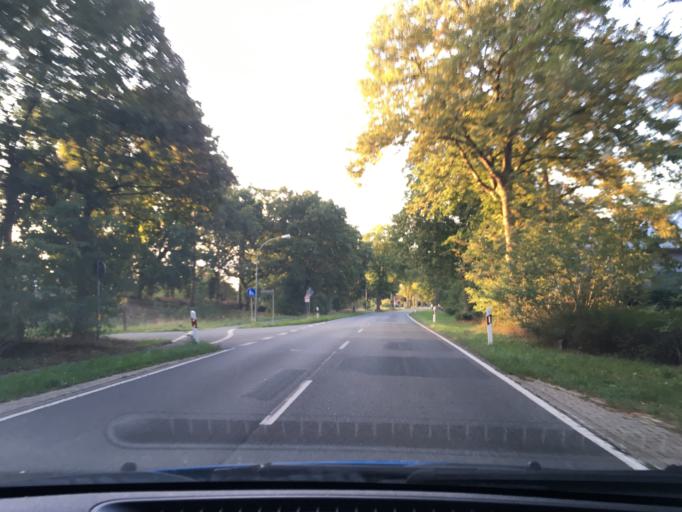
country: DE
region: Lower Saxony
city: Bleckede
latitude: 53.2790
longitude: 10.7413
